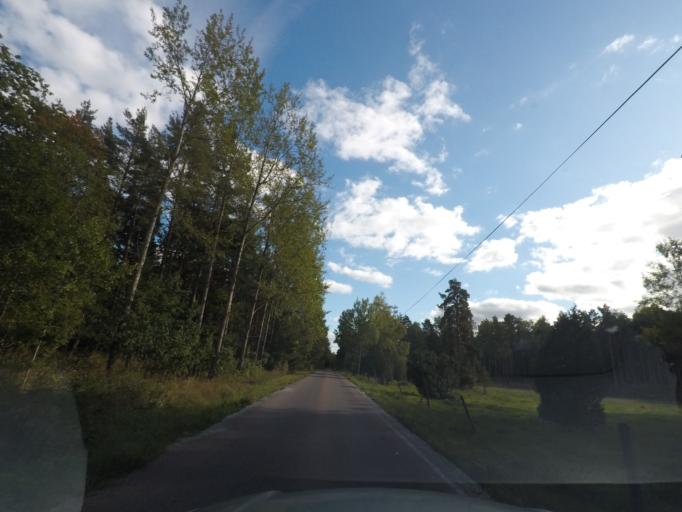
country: SE
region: Vaestmanland
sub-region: Hallstahammars Kommun
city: Kolback
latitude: 59.4949
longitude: 16.1903
